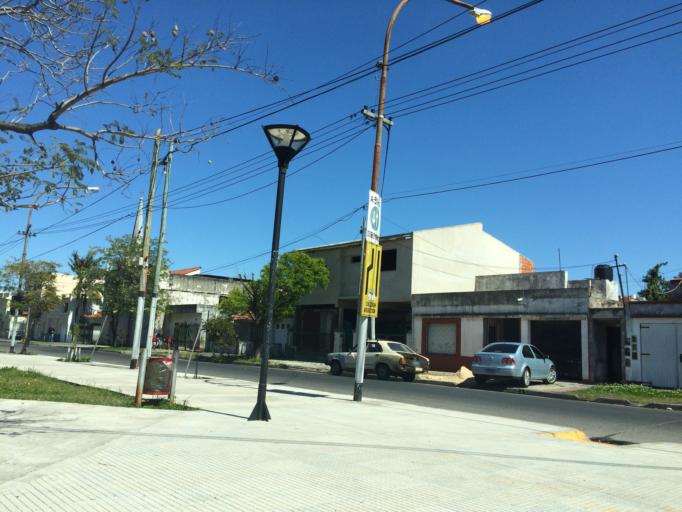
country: AR
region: Buenos Aires
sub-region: Partido de Lanus
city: Lanus
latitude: -34.7239
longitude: -58.3997
